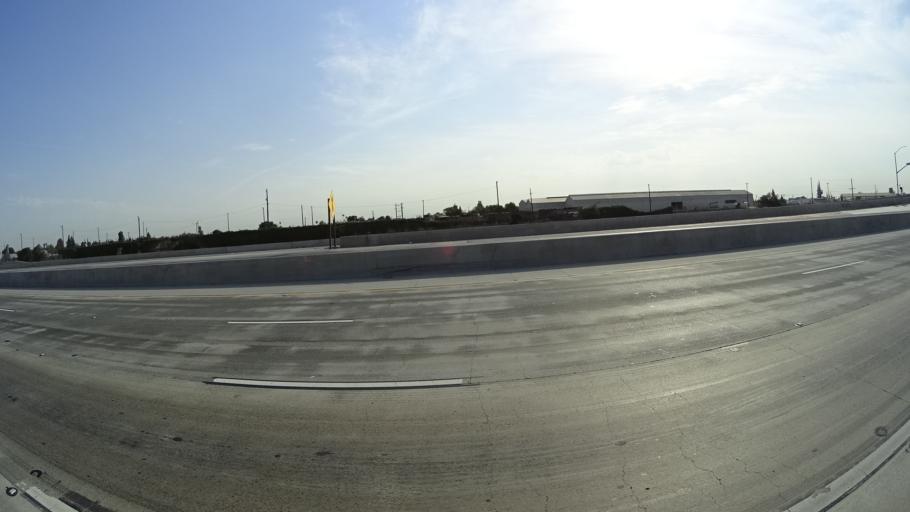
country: US
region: California
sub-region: Fresno County
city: West Park
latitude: 36.7740
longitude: -119.8407
